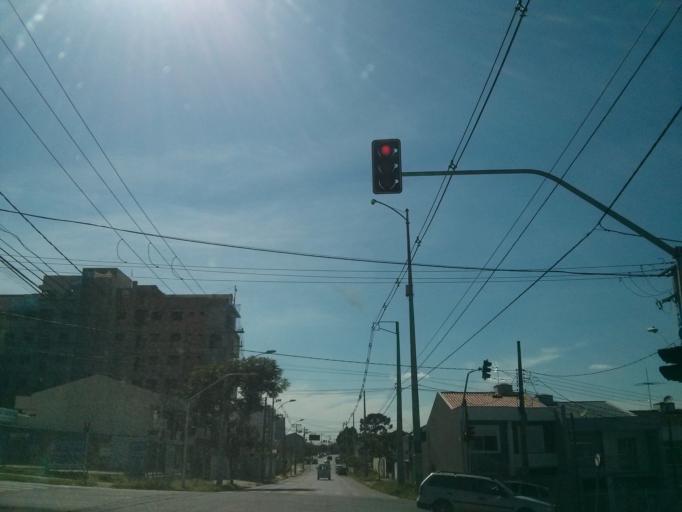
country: BR
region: Parana
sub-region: Sao Jose Dos Pinhais
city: Sao Jose dos Pinhais
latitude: -25.5438
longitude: -49.2049
